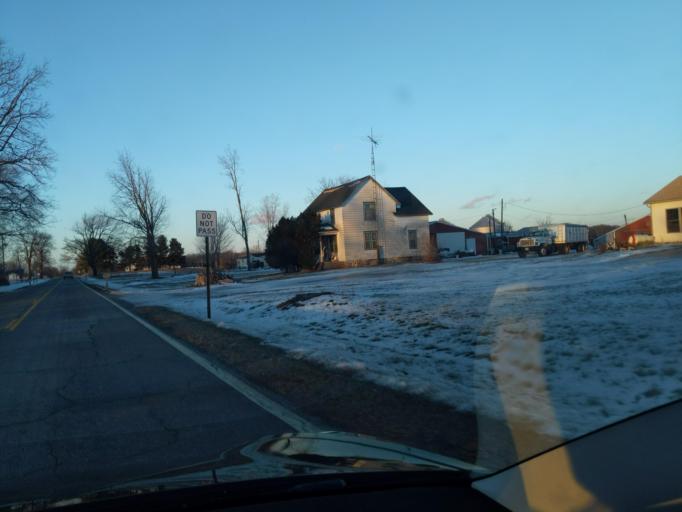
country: US
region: Michigan
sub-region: Ingham County
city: Stockbridge
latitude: 42.4504
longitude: -84.2584
